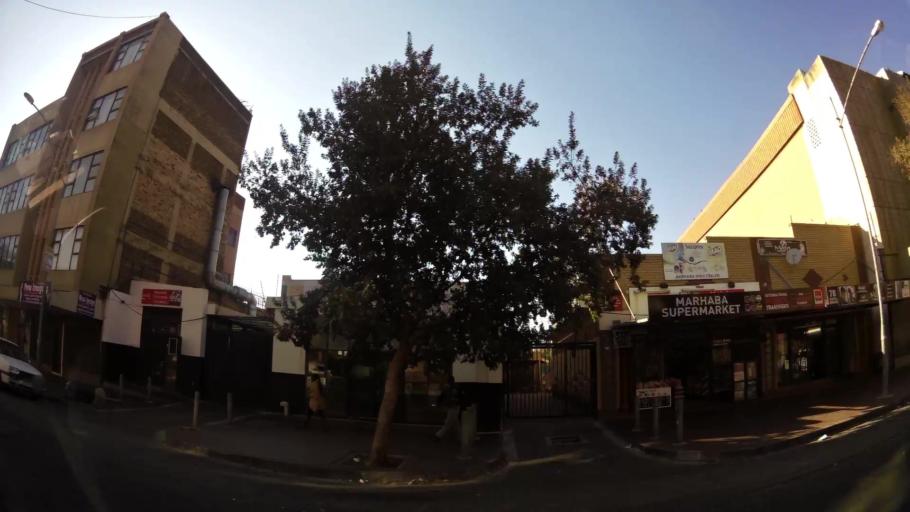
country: ZA
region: Gauteng
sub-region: City of Johannesburg Metropolitan Municipality
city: Johannesburg
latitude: -26.2028
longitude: 28.0223
